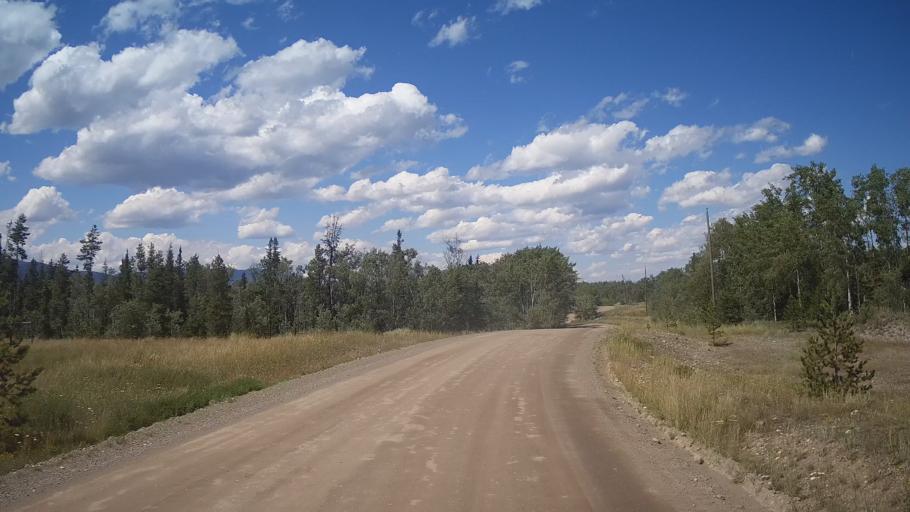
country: CA
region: British Columbia
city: Cache Creek
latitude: 51.2593
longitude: -121.6901
